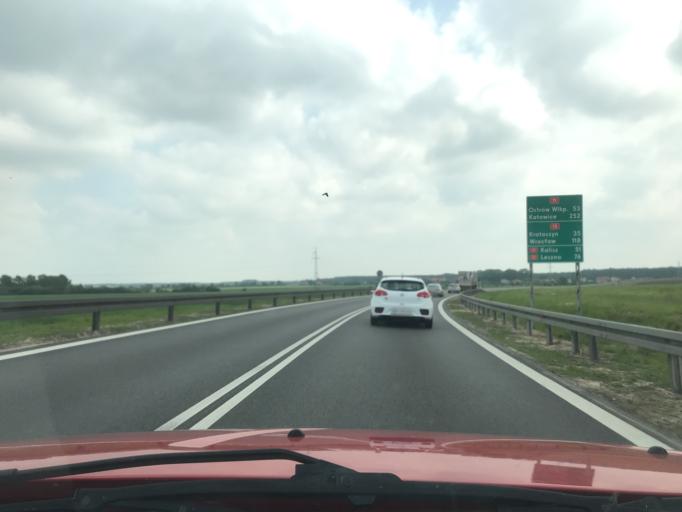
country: PL
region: Greater Poland Voivodeship
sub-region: Powiat jarocinski
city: Jarocin
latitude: 51.9764
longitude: 17.5247
